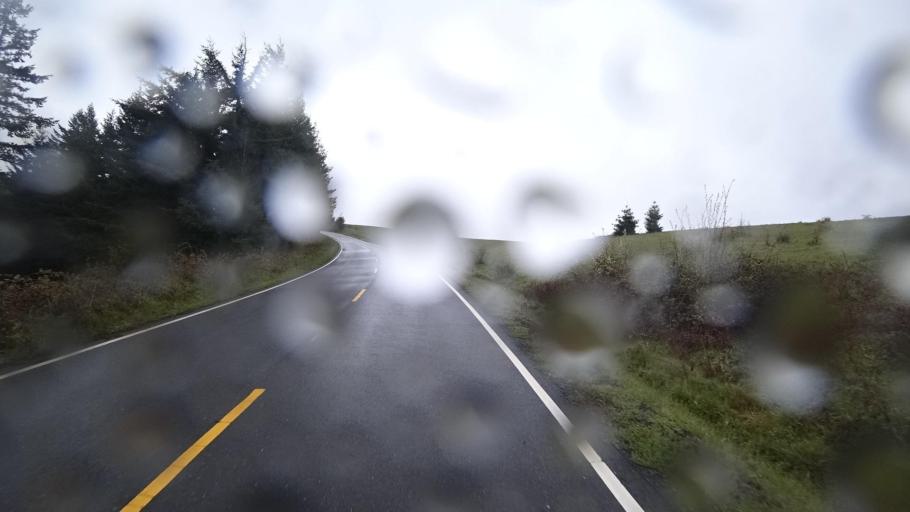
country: US
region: California
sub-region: Humboldt County
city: Westhaven-Moonstone
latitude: 41.1675
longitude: -123.9168
